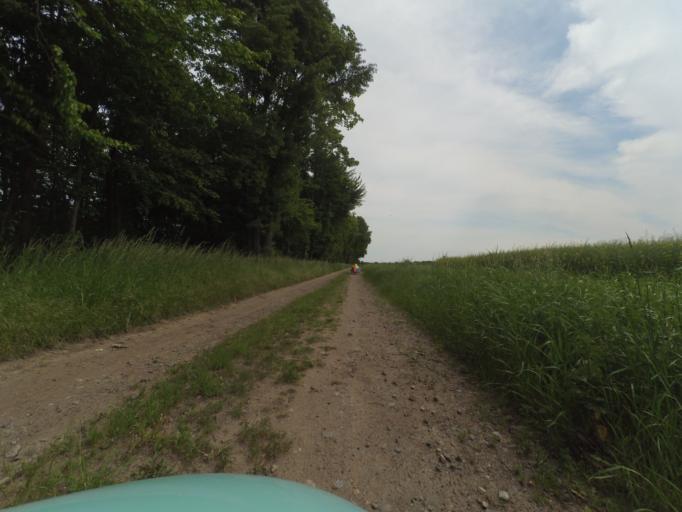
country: DE
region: Lower Saxony
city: Arpke
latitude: 52.3111
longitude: 10.1309
